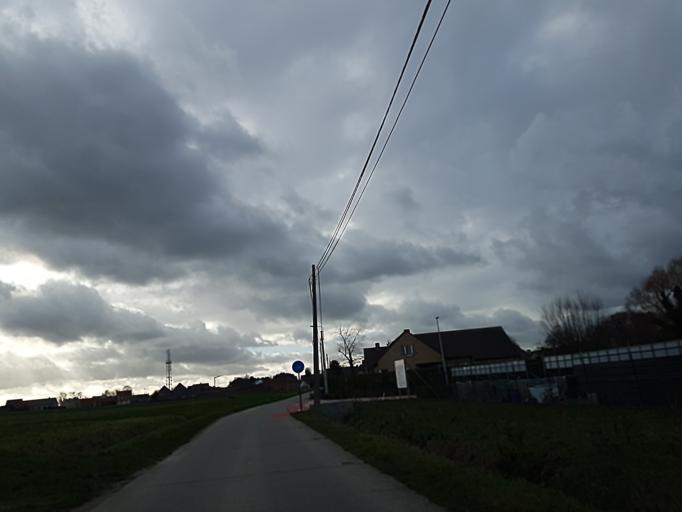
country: BE
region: Flanders
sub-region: Provincie Oost-Vlaanderen
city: Kruishoutem
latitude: 50.9024
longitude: 3.5343
